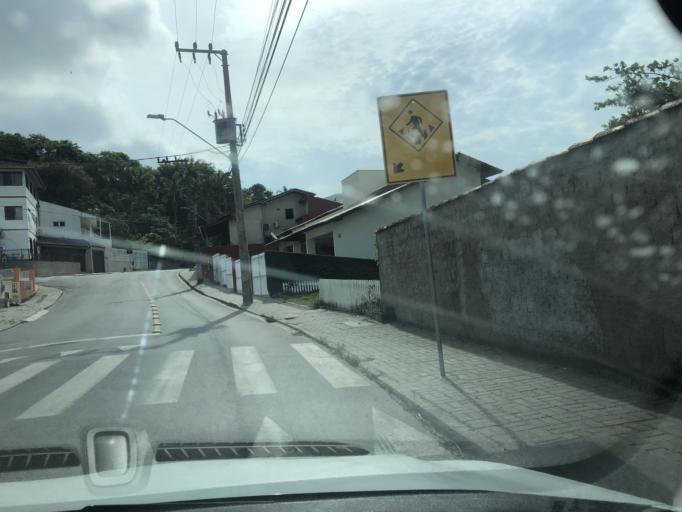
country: BR
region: Santa Catarina
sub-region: Sao Francisco Do Sul
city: Sao Francisco do Sul
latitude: -26.2304
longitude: -48.6186
